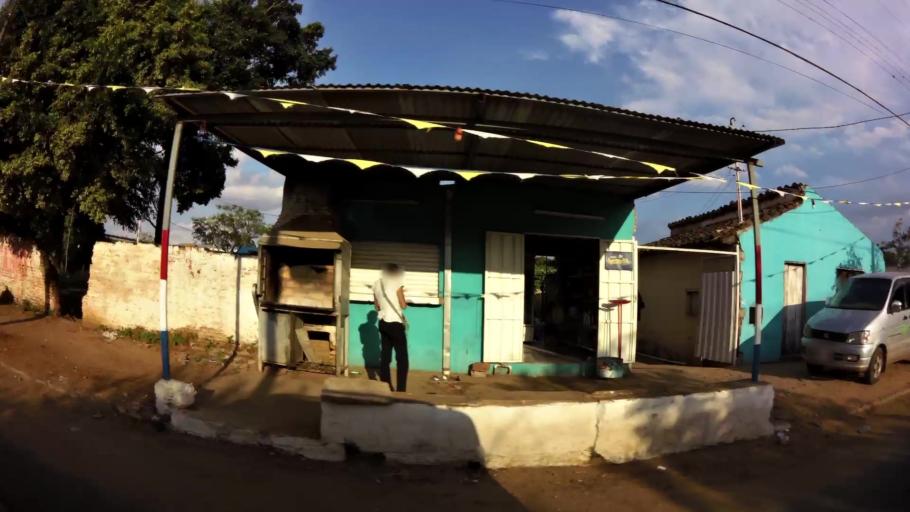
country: PY
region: Central
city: Fernando de la Mora
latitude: -25.3661
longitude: -57.5307
